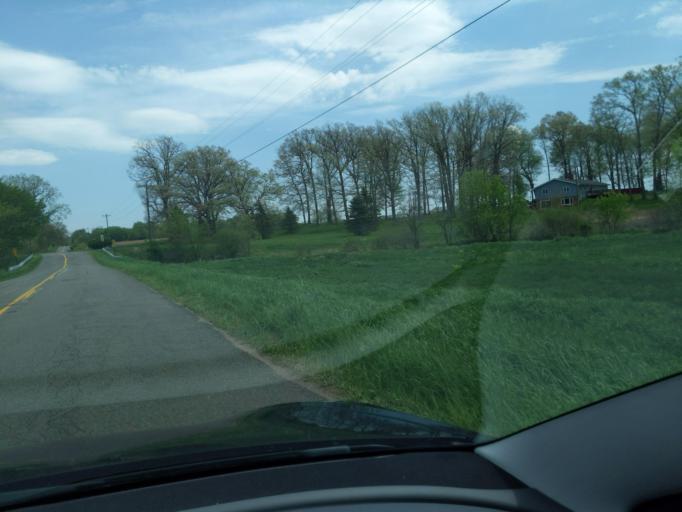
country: US
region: Michigan
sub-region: Ingham County
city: Stockbridge
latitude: 42.4540
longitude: -84.2171
